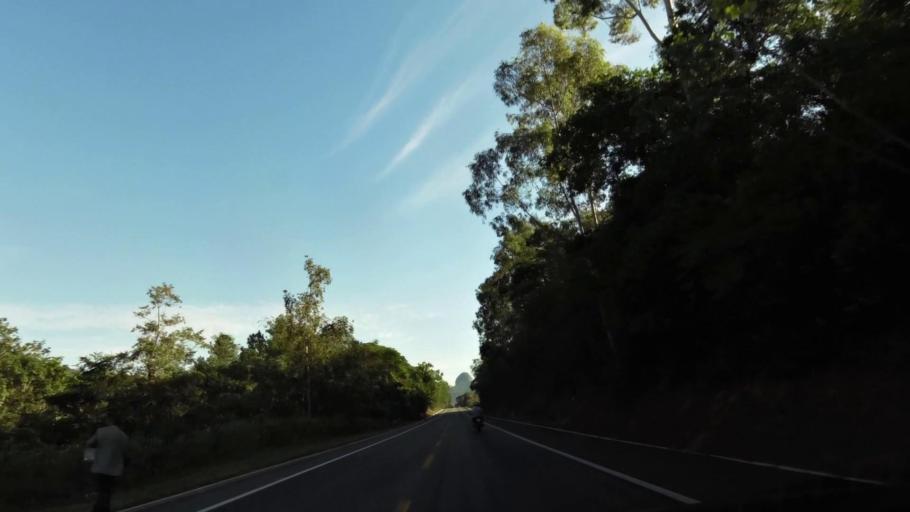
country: BR
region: Espirito Santo
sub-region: Guarapari
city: Guarapari
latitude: -20.5531
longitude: -40.4808
